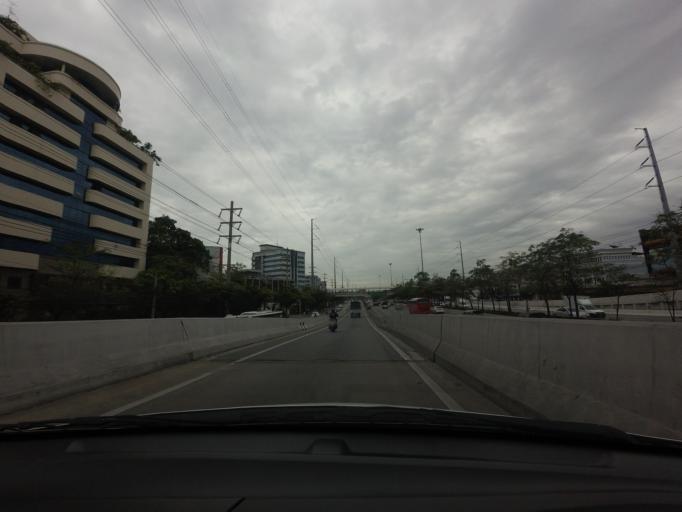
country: TH
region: Bangkok
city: Chom Thong
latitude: 13.6759
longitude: 100.4614
